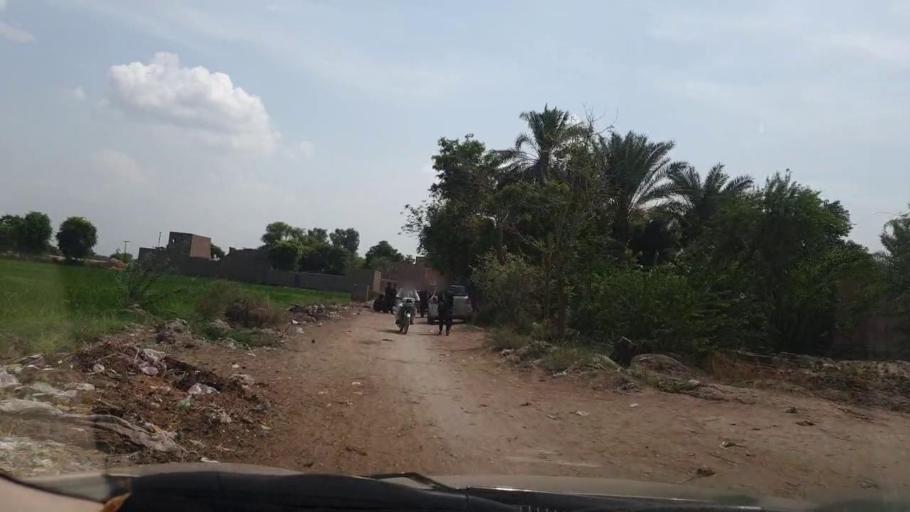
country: PK
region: Sindh
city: Larkana
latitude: 27.5835
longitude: 68.1669
